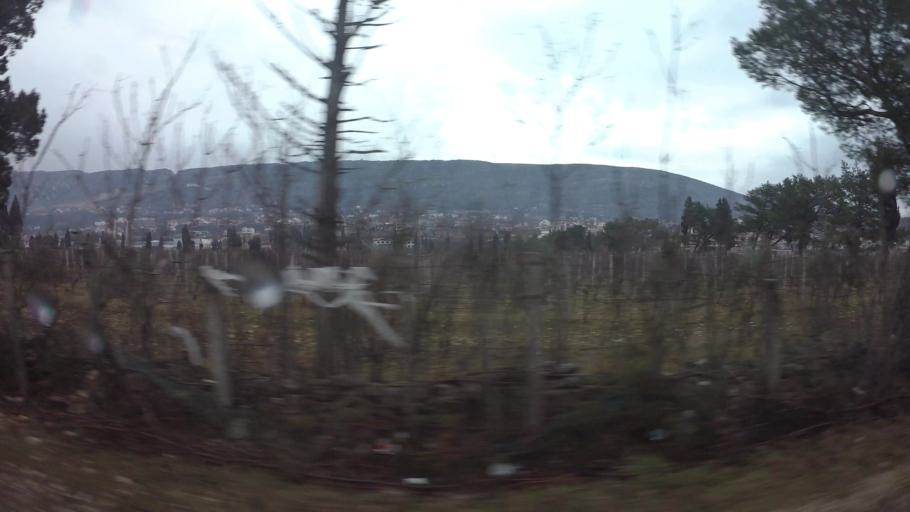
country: BA
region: Federation of Bosnia and Herzegovina
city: Rodoc
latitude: 43.2987
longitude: 17.8419
